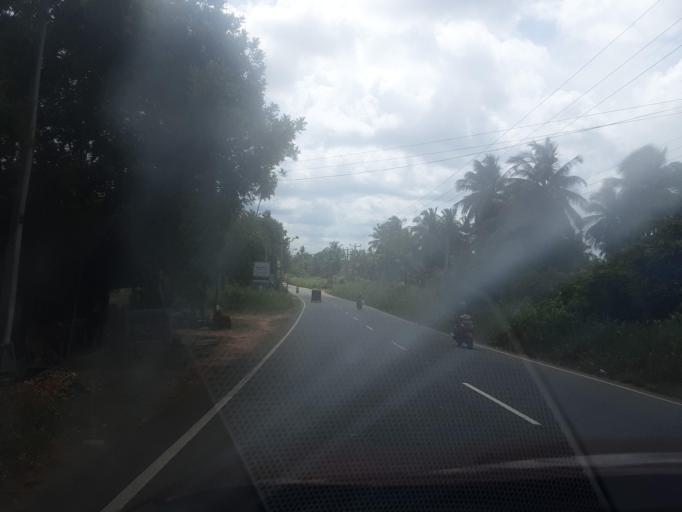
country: LK
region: North Western
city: Kuliyapitiya
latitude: 7.4817
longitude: 79.9874
